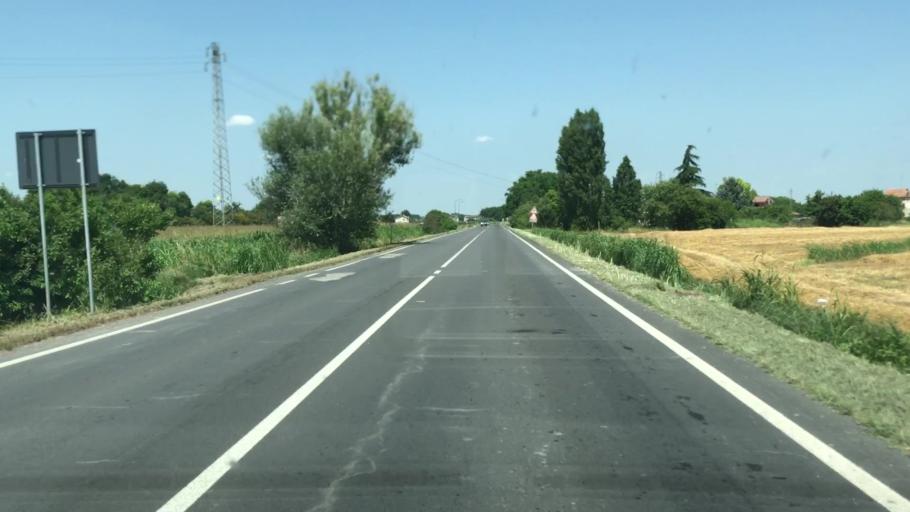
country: IT
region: Veneto
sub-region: Provincia di Rovigo
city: Castelmassa
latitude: 45.0301
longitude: 11.3076
